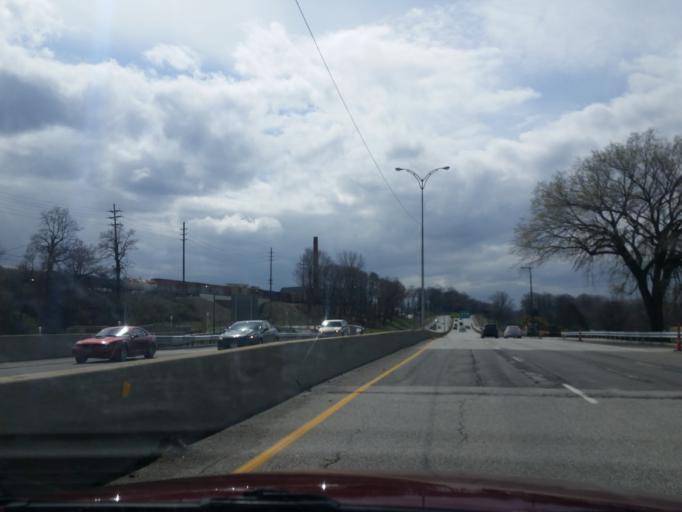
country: US
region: Ohio
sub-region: Cuyahoga County
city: Cleveland
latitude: 41.4902
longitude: -81.7326
